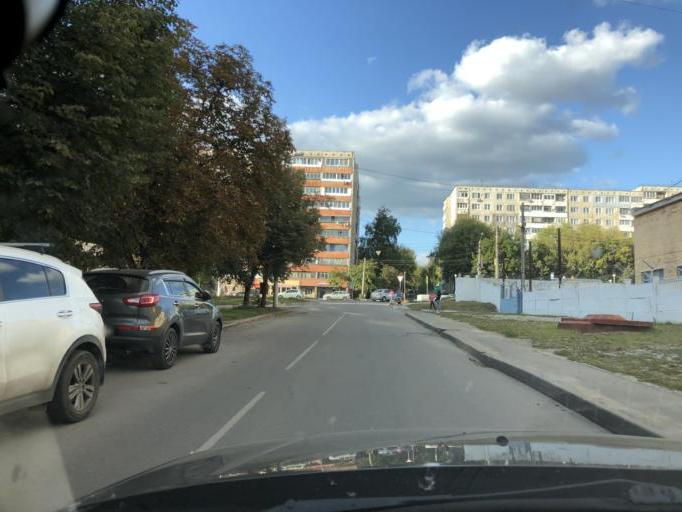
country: RU
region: Tula
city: Tula
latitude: 54.2141
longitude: 37.6116
